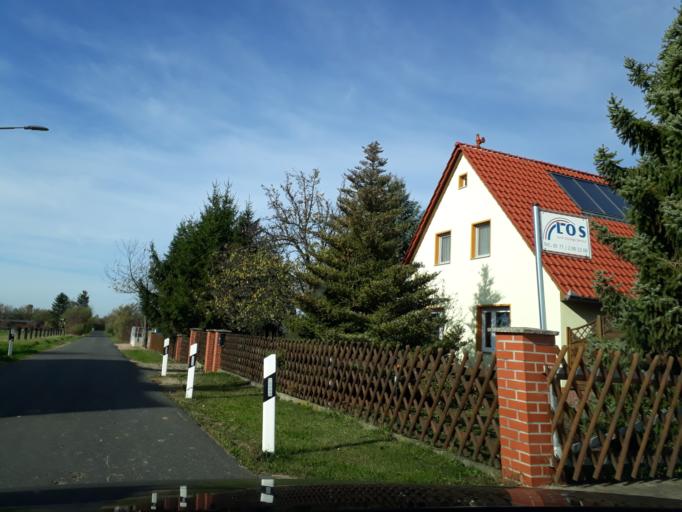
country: DE
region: Saxony
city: Niederstriegis
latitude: 51.1017
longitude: 13.1519
